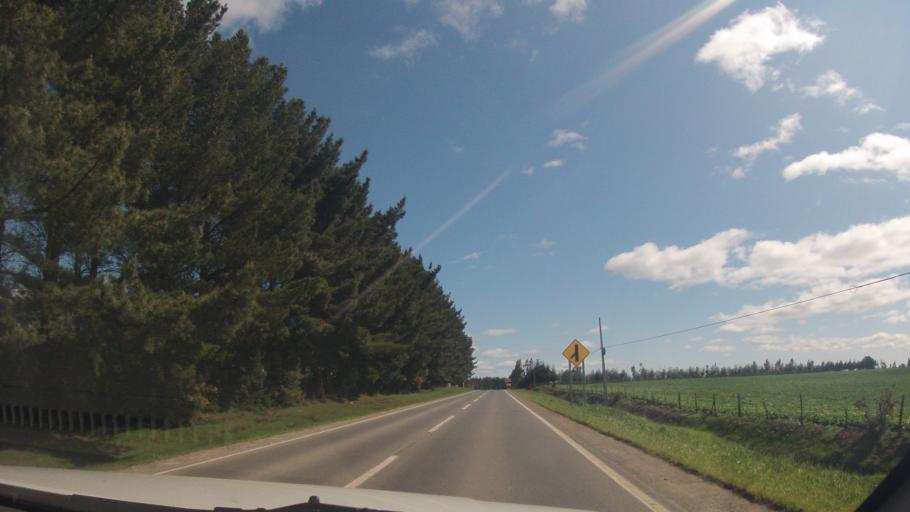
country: CL
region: Araucania
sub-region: Provincia de Malleco
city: Traiguen
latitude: -38.2637
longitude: -72.6426
